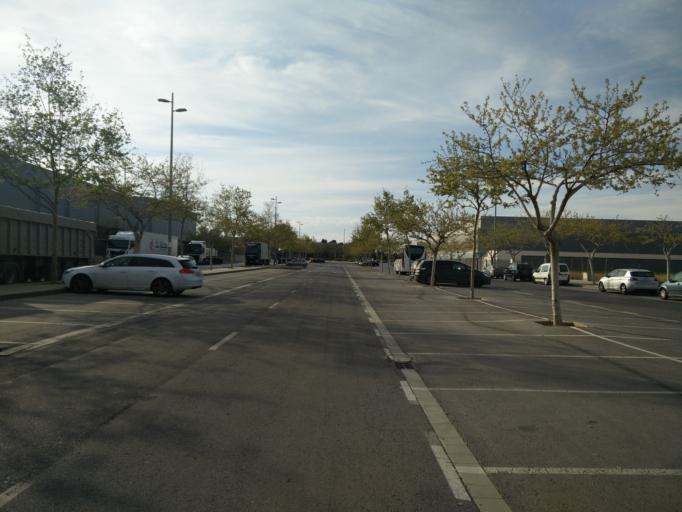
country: ES
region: Valencia
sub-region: Provincia de Castello
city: Castello de la Plana
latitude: 39.9804
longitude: -0.0621
